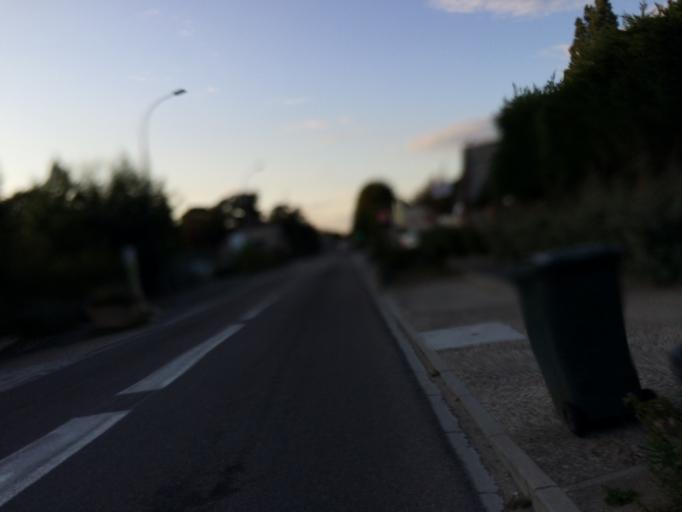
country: FR
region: Ile-de-France
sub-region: Departement de l'Essonne
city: Orsay
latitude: 48.6683
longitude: 2.1965
